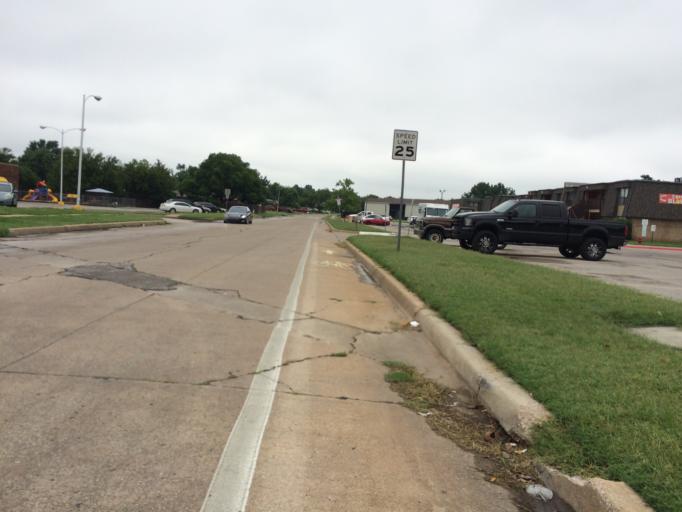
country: US
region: Oklahoma
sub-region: Cleveland County
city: Norman
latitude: 35.2041
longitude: -97.4200
